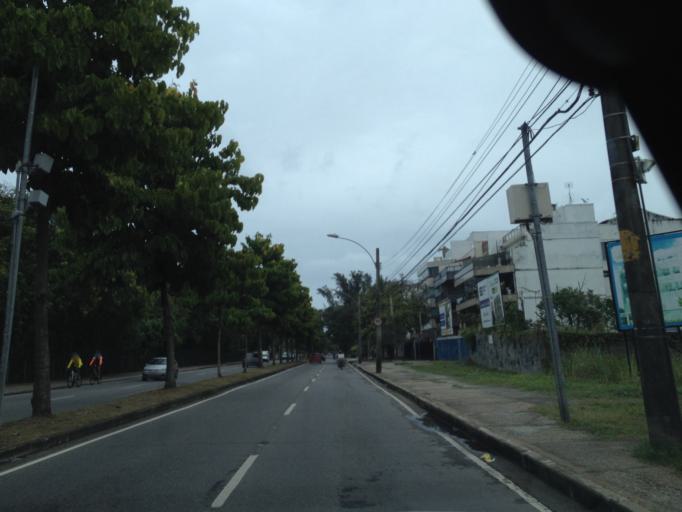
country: BR
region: Rio de Janeiro
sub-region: Nilopolis
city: Nilopolis
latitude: -23.0160
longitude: -43.4484
